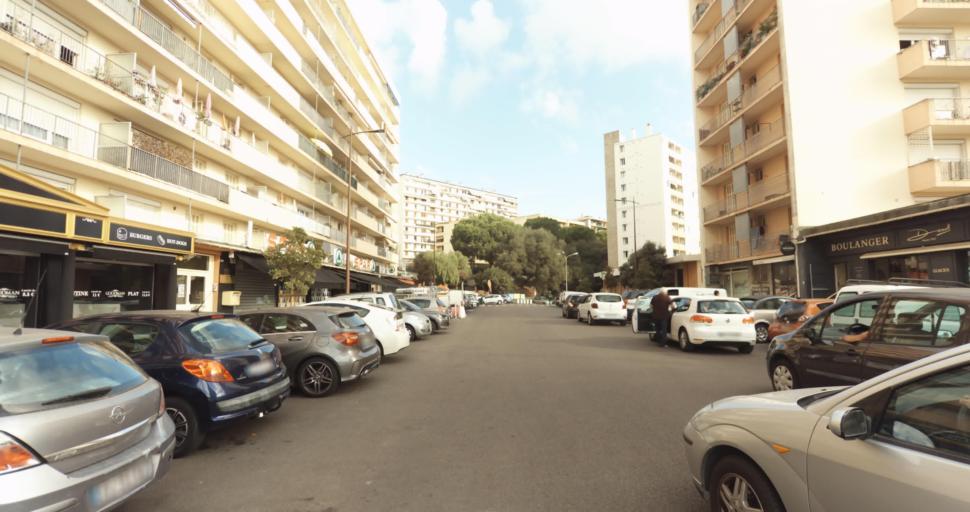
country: FR
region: Corsica
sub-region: Departement de la Corse-du-Sud
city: Ajaccio
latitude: 41.9304
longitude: 8.7333
